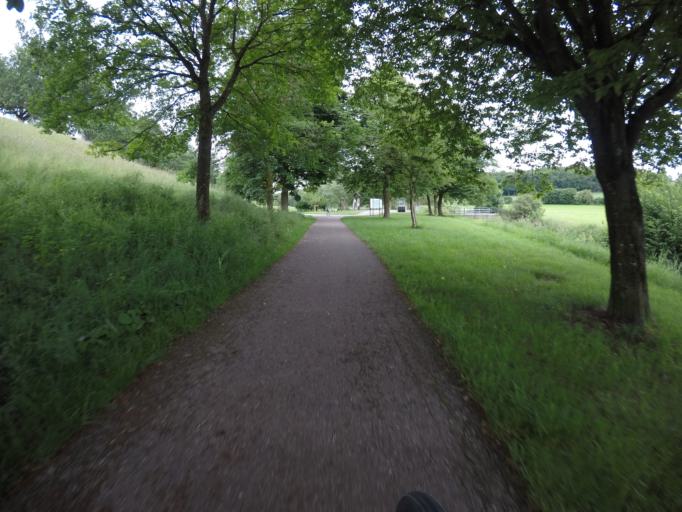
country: DE
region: Baden-Wuerttemberg
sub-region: Tuebingen Region
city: Westerstetten
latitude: 48.5187
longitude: 9.9629
